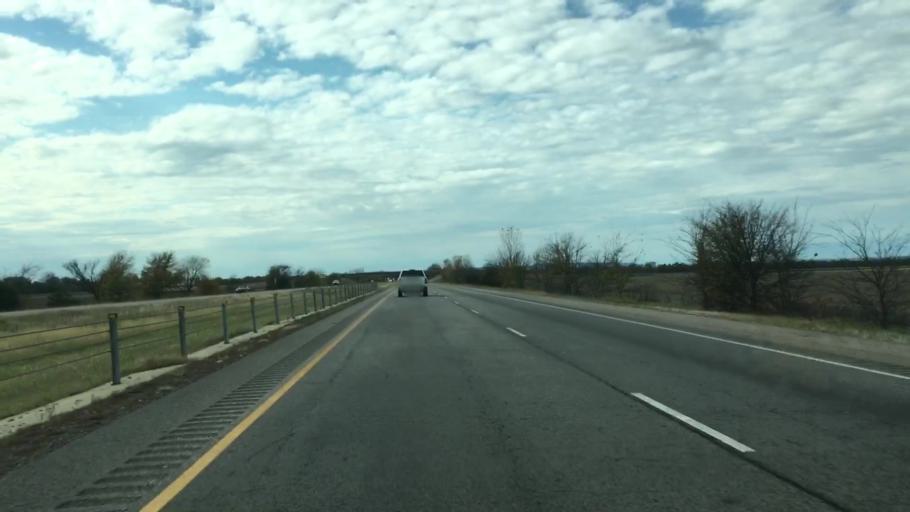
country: US
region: Arkansas
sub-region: Conway County
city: Morrilton
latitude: 35.1891
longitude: -92.7820
